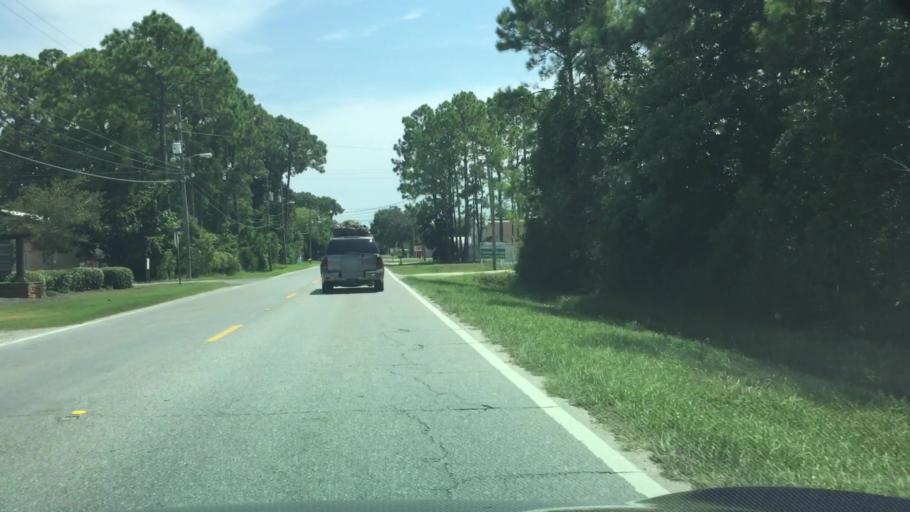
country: US
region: Florida
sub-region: Bay County
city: Panama City Beach
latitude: 30.1858
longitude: -85.7927
